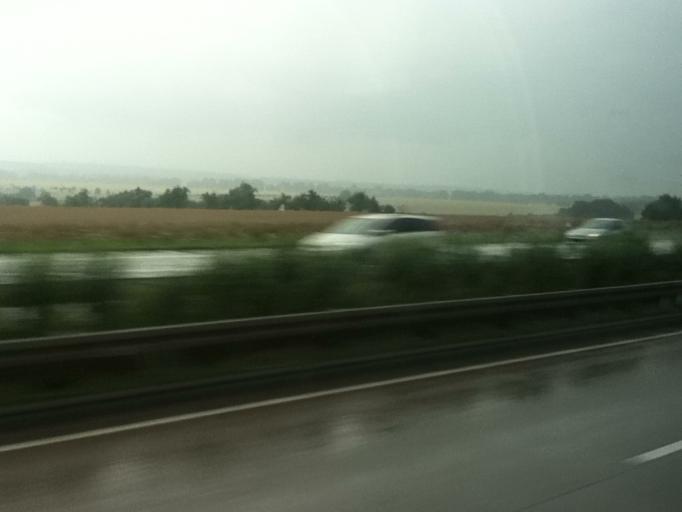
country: DE
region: Thuringia
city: Mechterstadt
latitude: 50.9276
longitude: 10.5109
